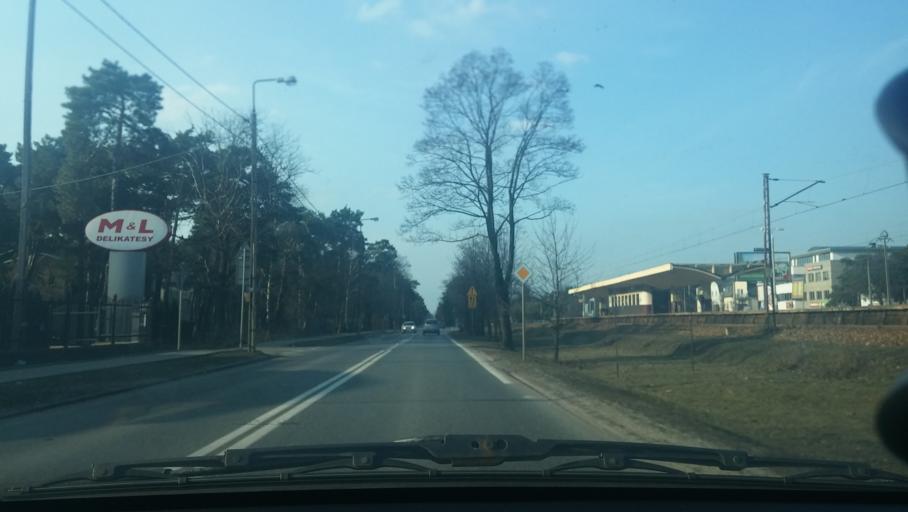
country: PL
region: Masovian Voivodeship
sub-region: Warszawa
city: Wawer
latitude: 52.1721
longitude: 21.2003
